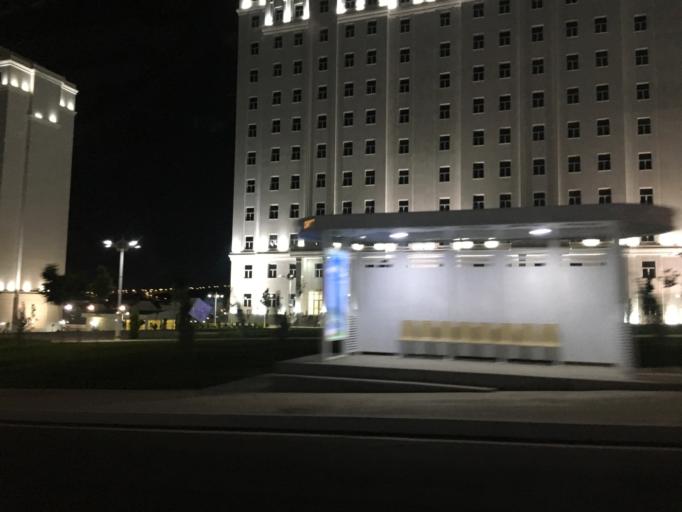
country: TM
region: Ahal
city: Ashgabat
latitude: 37.9408
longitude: 58.3488
